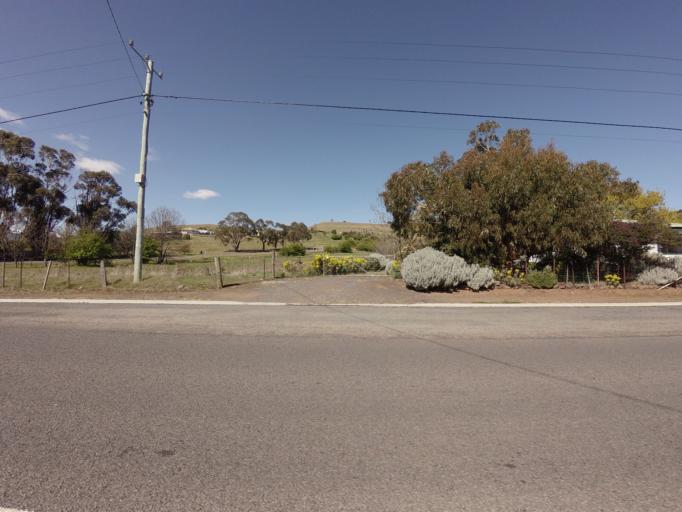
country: AU
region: Tasmania
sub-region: Derwent Valley
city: New Norfolk
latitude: -42.5575
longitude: 146.8334
